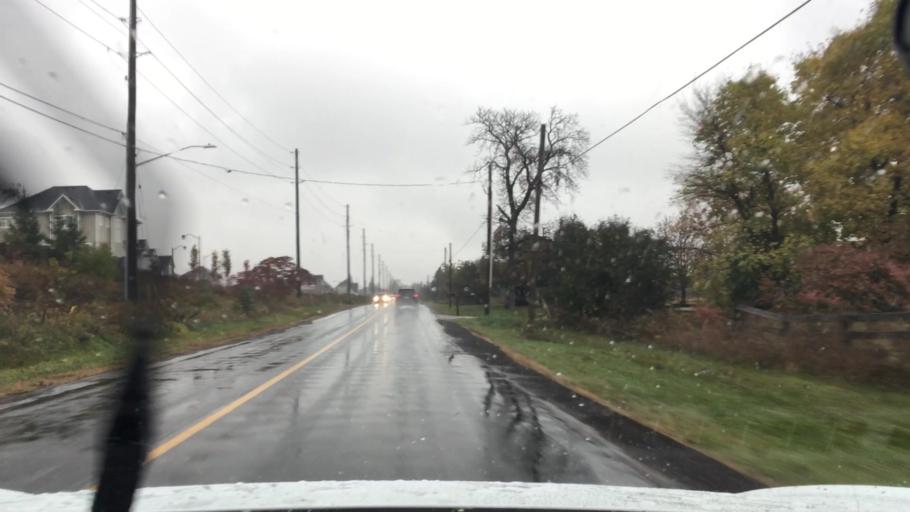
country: CA
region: Ontario
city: Oshawa
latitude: 43.9536
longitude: -78.8341
